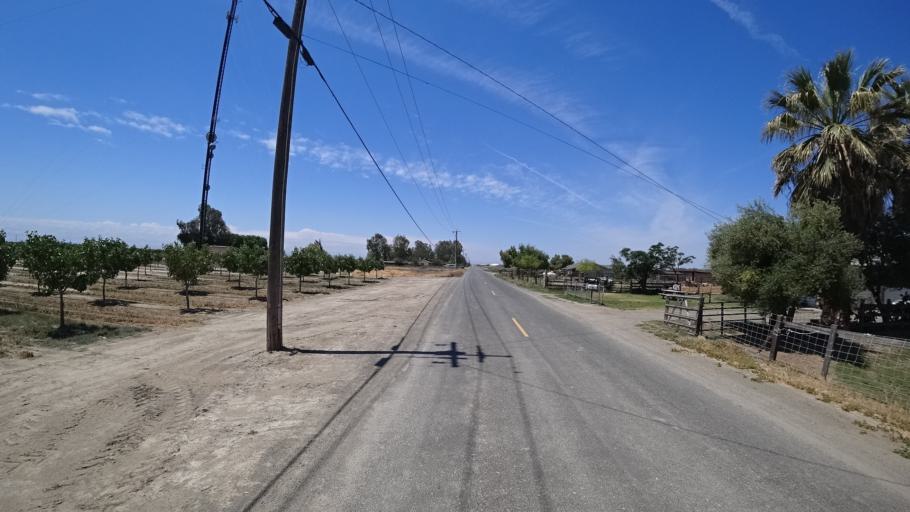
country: US
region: California
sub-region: Kings County
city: Stratford
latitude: 36.2330
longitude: -119.7879
